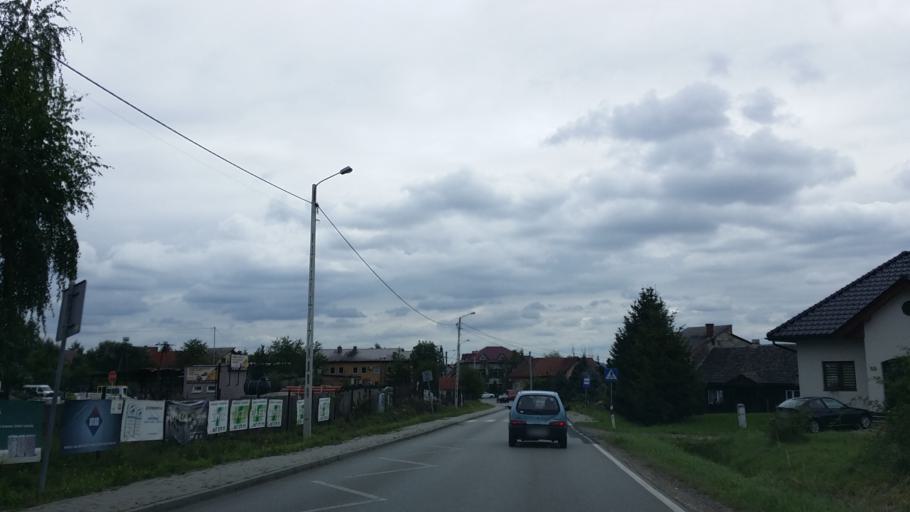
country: PL
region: Lesser Poland Voivodeship
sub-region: Powiat wadowicki
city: Tomice
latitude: 49.8911
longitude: 19.4698
